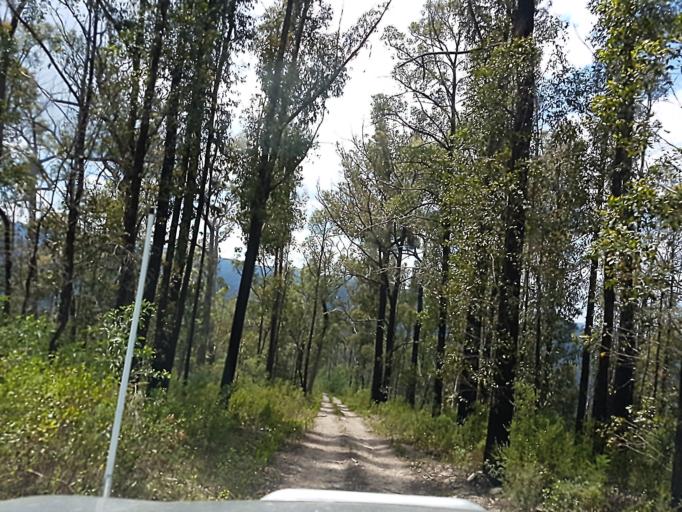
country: AU
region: Victoria
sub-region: East Gippsland
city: Lakes Entrance
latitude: -37.3463
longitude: 148.3508
